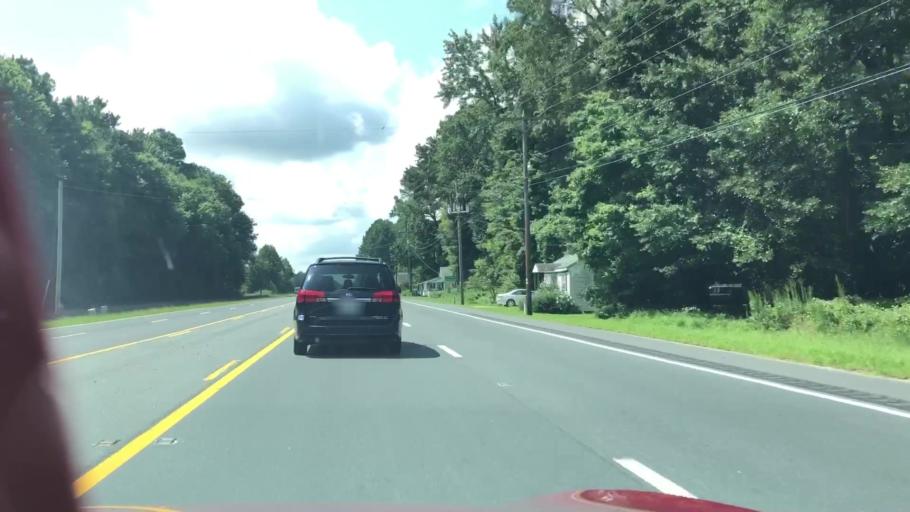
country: US
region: Virginia
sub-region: Accomack County
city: Onancock
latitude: 37.6569
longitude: -75.7380
